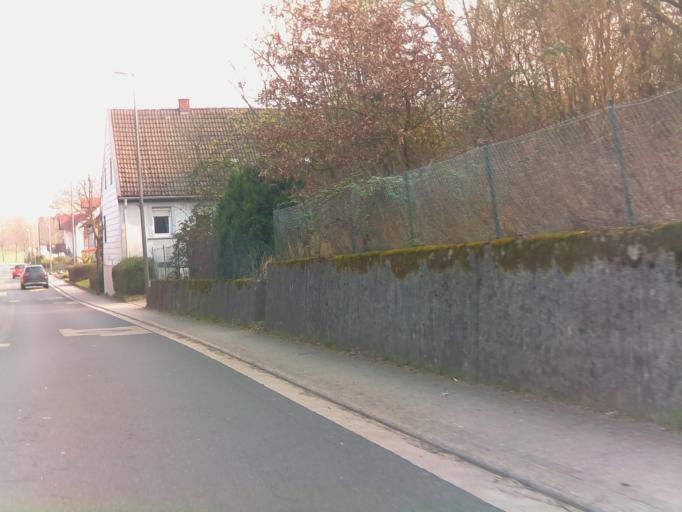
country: DE
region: Rheinland-Pfalz
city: Ruthweiler
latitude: 49.5504
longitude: 7.3699
